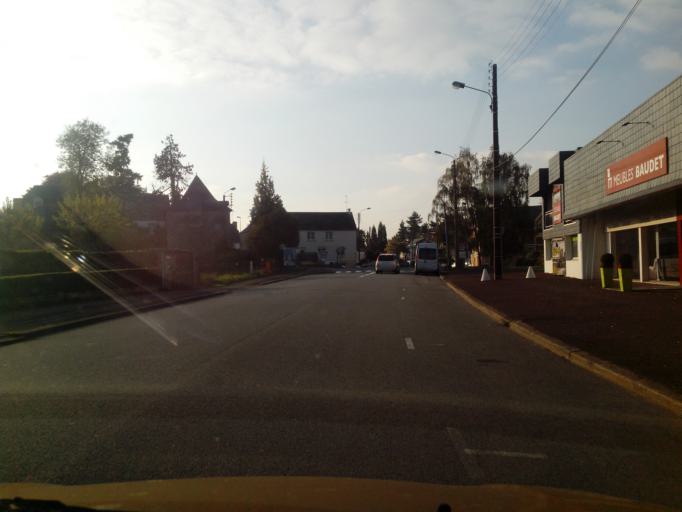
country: FR
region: Brittany
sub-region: Departement du Morbihan
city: Ploermel
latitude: 47.9326
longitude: -2.3921
